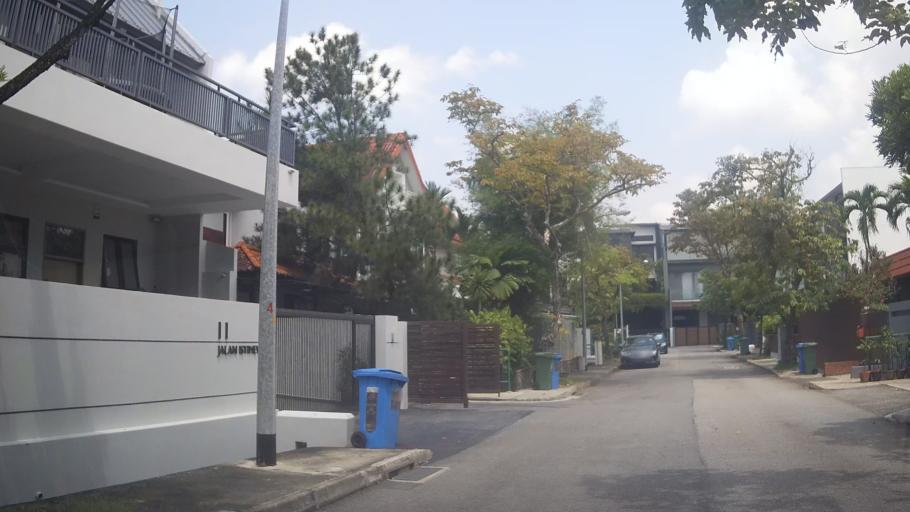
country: SG
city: Singapore
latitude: 1.3163
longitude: 103.7872
